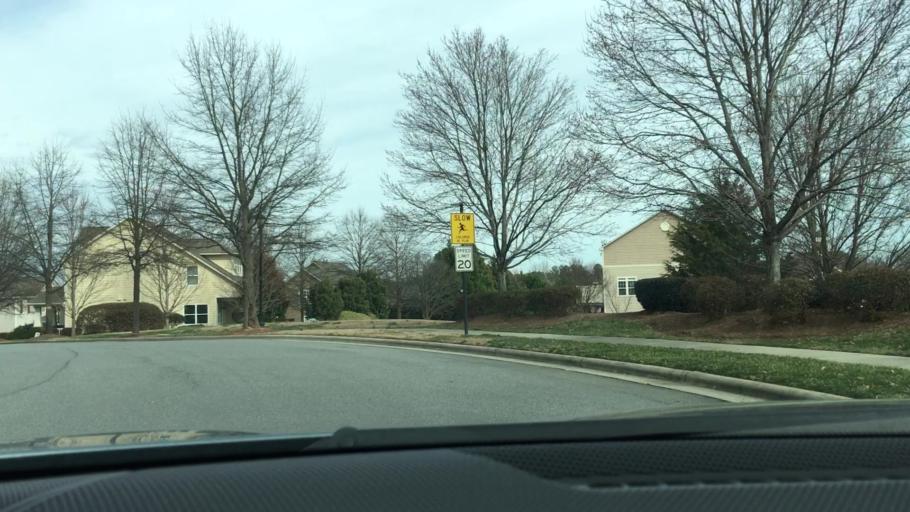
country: US
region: North Carolina
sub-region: Mecklenburg County
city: Cornelius
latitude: 35.4663
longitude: -80.8876
